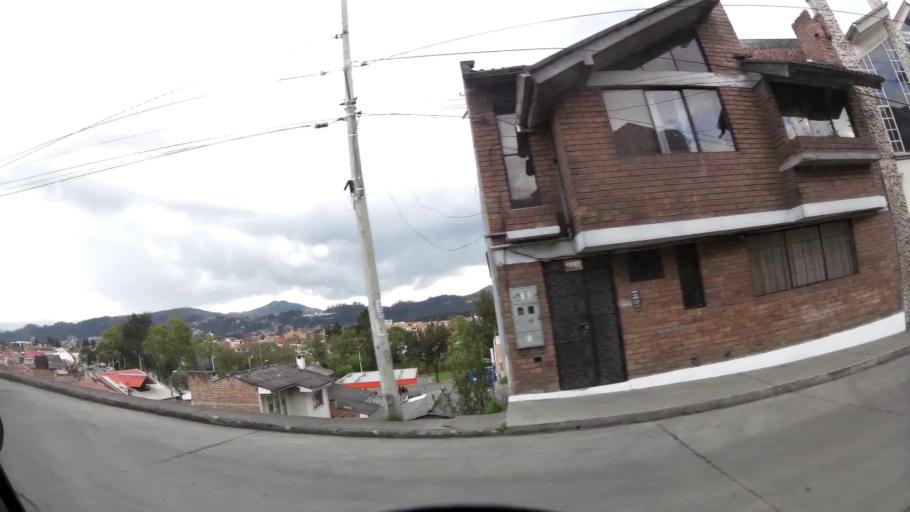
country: EC
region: Azuay
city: Cuenca
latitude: -2.8954
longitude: -79.0140
